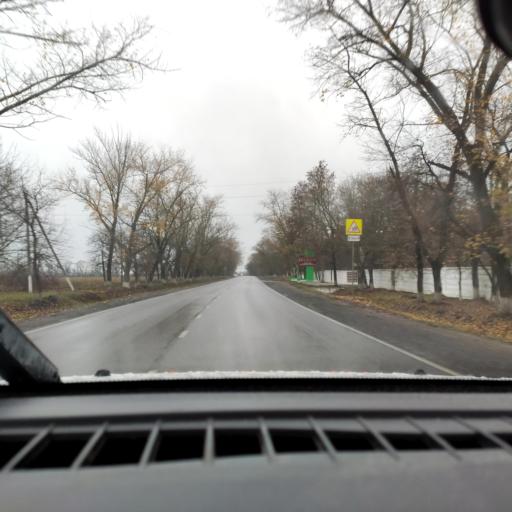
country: RU
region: Belgorod
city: Alekseyevka
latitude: 50.6637
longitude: 38.6670
